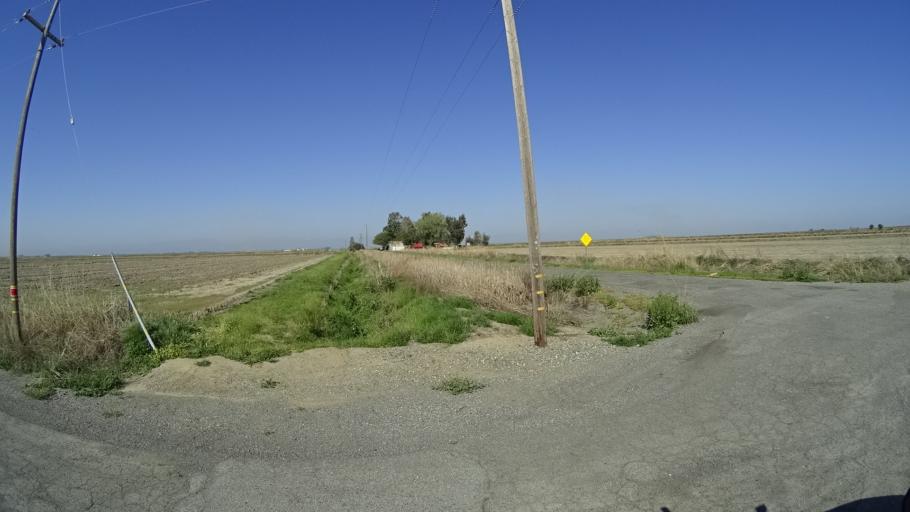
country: US
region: California
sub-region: Glenn County
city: Willows
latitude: 39.6019
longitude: -122.0884
